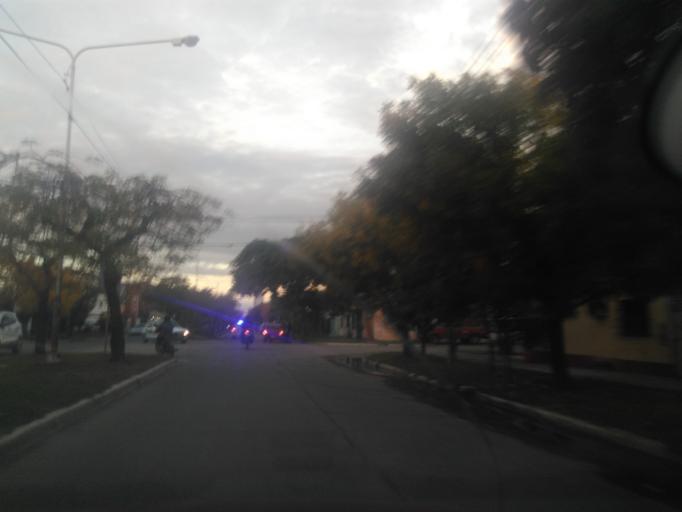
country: AR
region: Chaco
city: Resistencia
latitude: -27.4673
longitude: -58.9957
